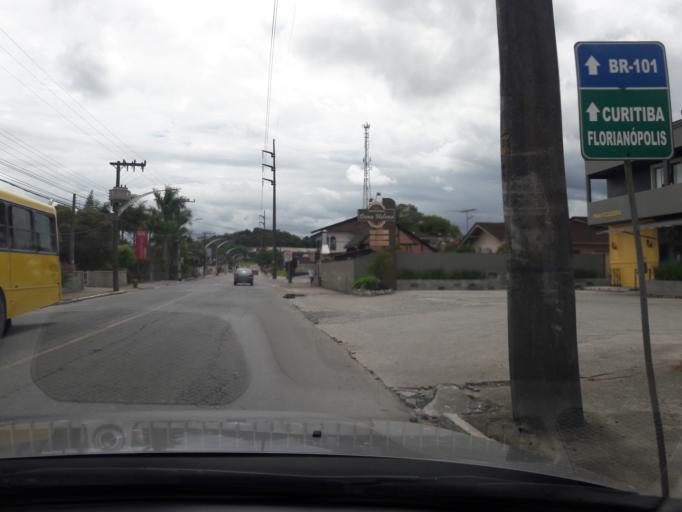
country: BR
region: Santa Catarina
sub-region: Joinville
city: Joinville
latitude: -26.3244
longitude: -48.8621
